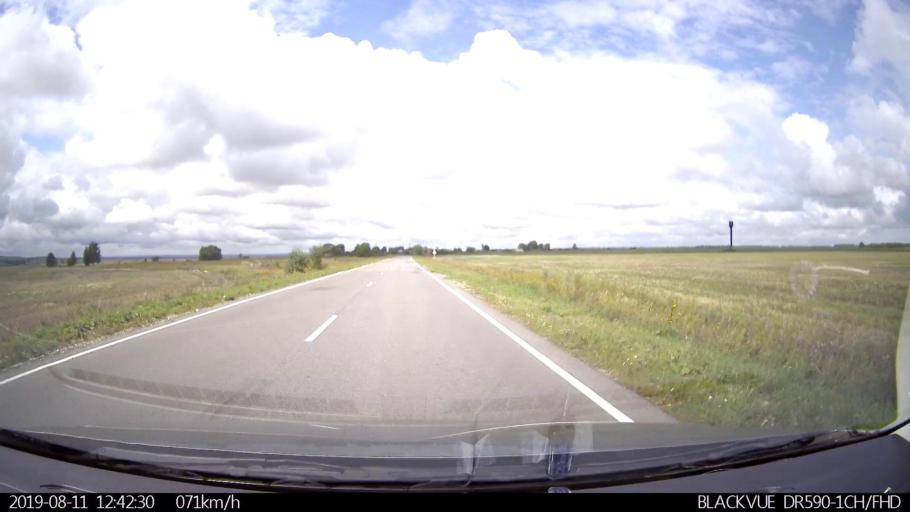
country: RU
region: Ulyanovsk
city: Ignatovka
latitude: 53.8469
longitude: 47.7504
